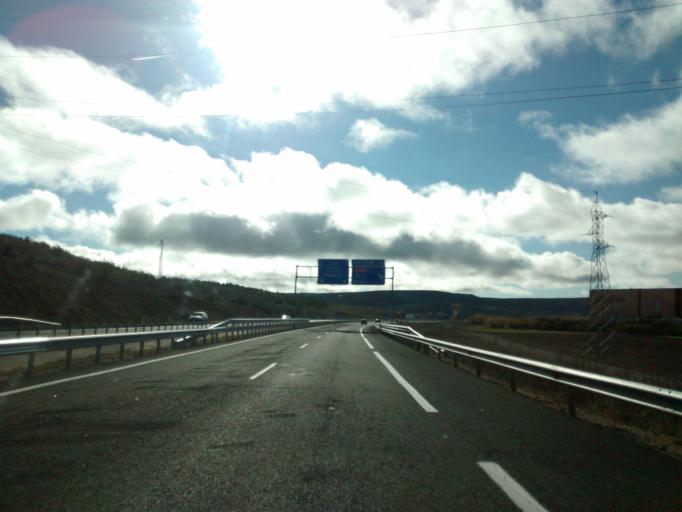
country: ES
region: Castille and Leon
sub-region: Provincia de Palencia
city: Aguilar de Campoo
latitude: 42.7932
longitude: -4.2370
